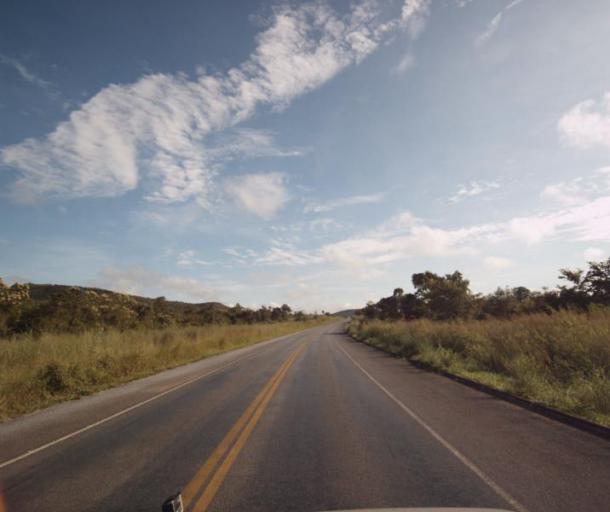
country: BR
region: Goias
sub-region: Pirenopolis
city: Pirenopolis
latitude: -15.5565
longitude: -48.6229
